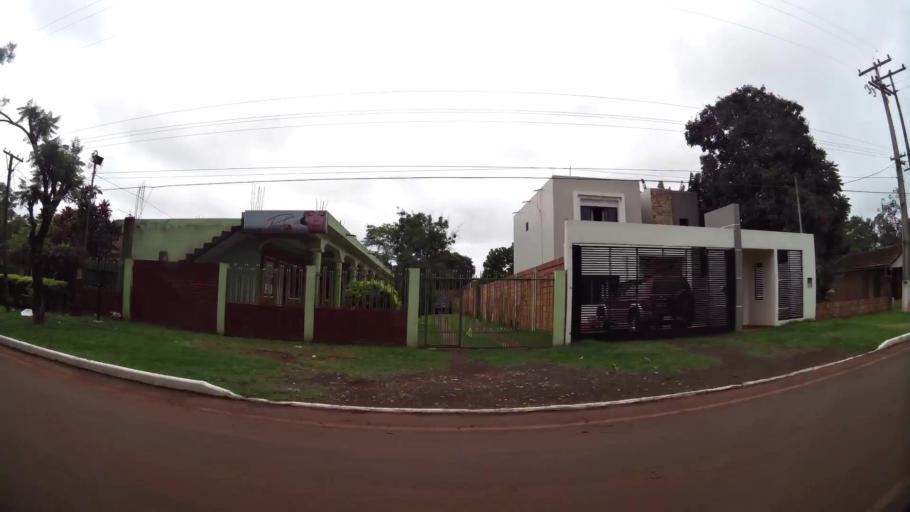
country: PY
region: Alto Parana
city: Ciudad del Este
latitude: -25.4848
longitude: -54.7605
